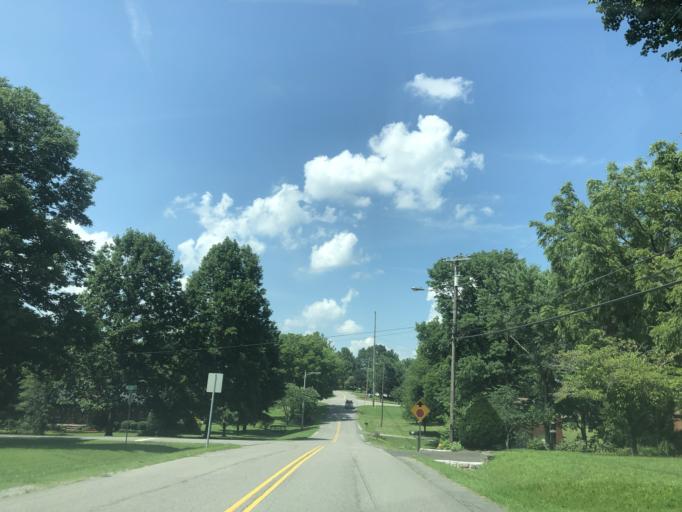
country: US
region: Tennessee
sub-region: Davidson County
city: Lakewood
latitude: 36.1831
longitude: -86.6715
